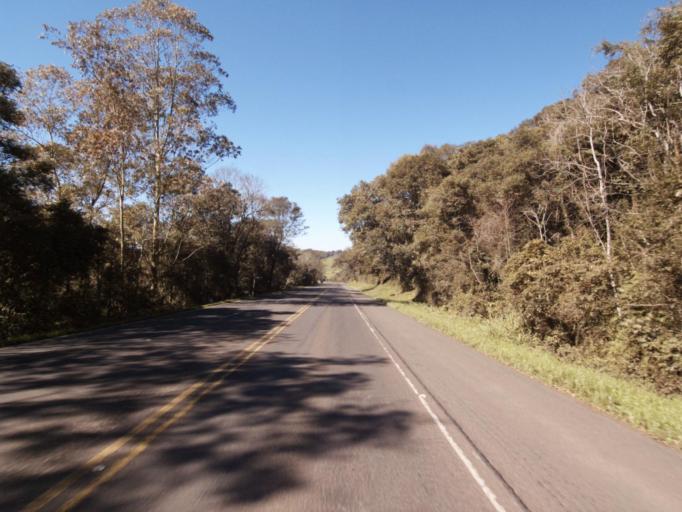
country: BR
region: Santa Catarina
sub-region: Sao Lourenco Do Oeste
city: Sao Lourenco dOeste
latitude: -26.8212
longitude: -53.1537
